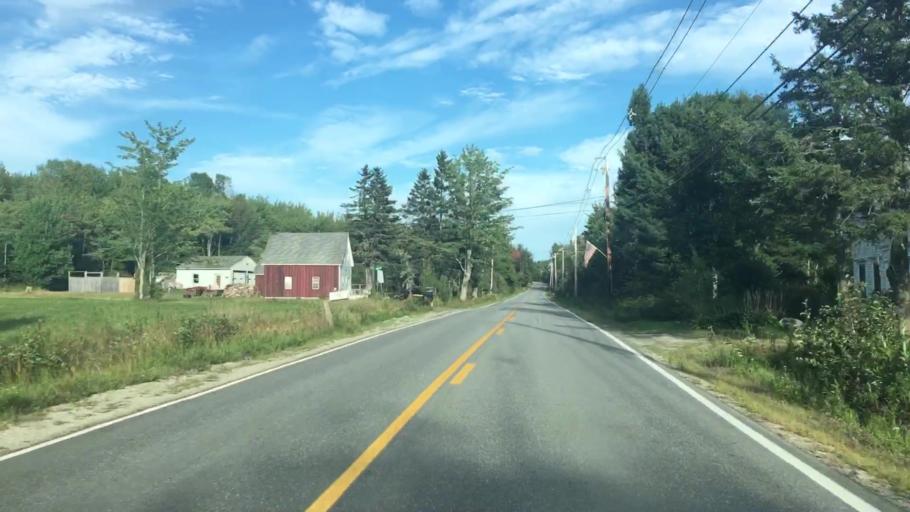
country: US
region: Maine
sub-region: Hancock County
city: Trenton
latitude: 44.4376
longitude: -68.3894
